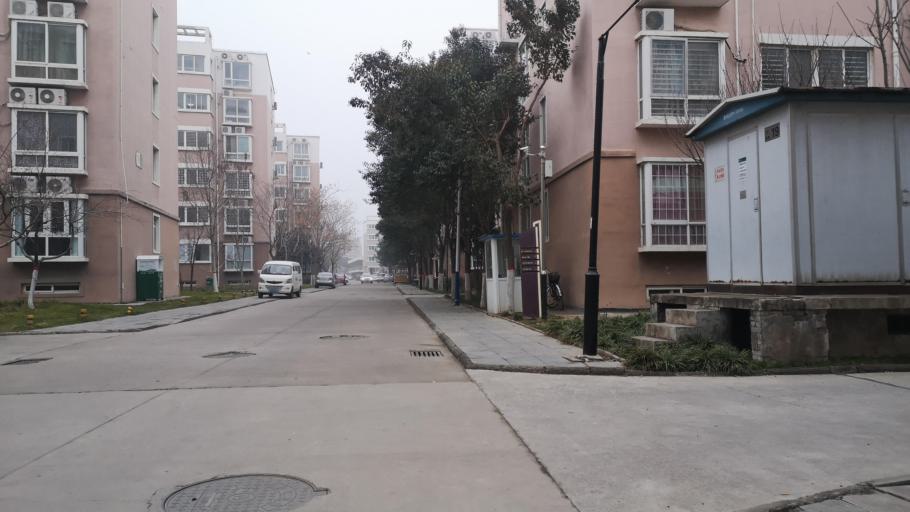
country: CN
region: Henan Sheng
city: Zhongyuanlu
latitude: 35.7856
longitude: 115.0884
